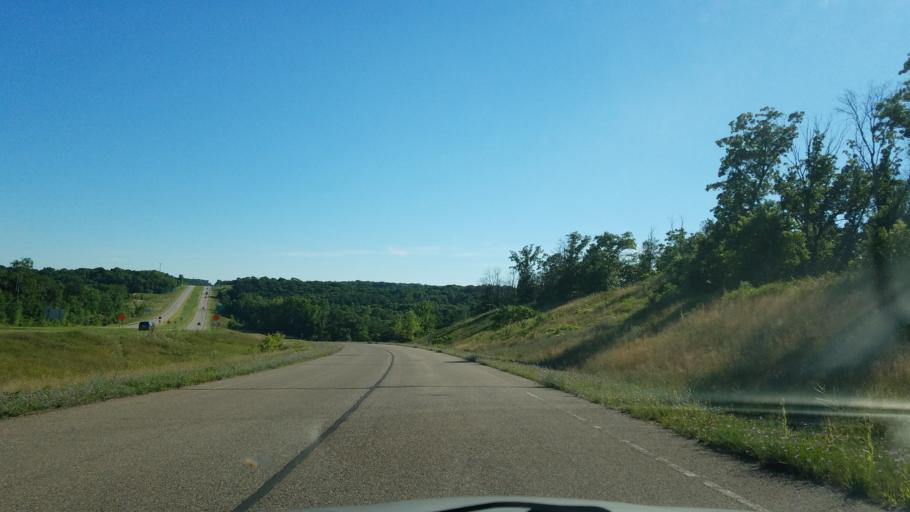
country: US
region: Wisconsin
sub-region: Saint Croix County
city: Somerset
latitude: 45.1055
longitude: -92.7291
